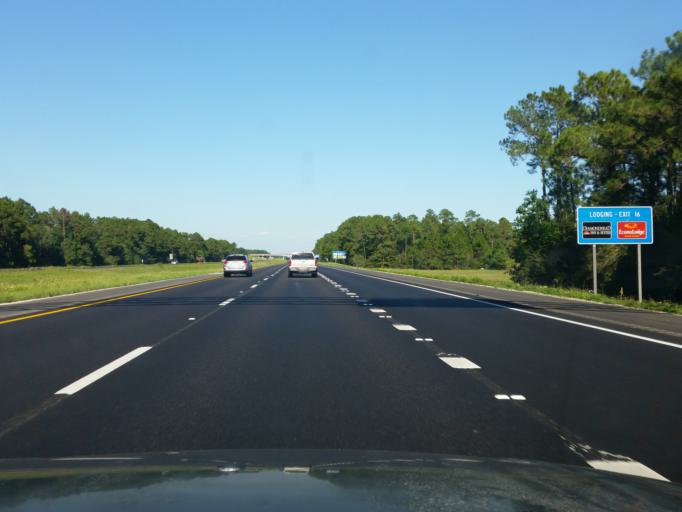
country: US
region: Mississippi
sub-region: Hancock County
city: Diamondhead
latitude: 30.3686
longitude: -89.3893
